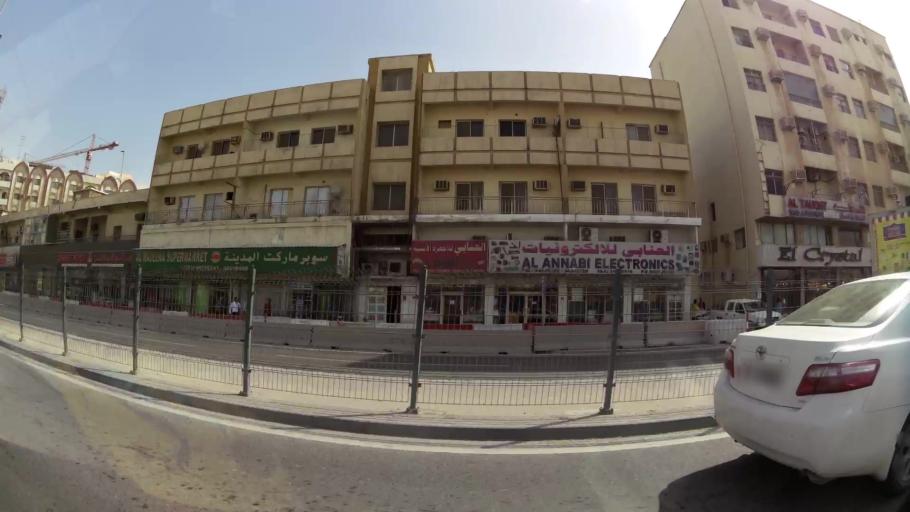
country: QA
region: Baladiyat ad Dawhah
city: Doha
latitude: 25.2824
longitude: 51.5176
